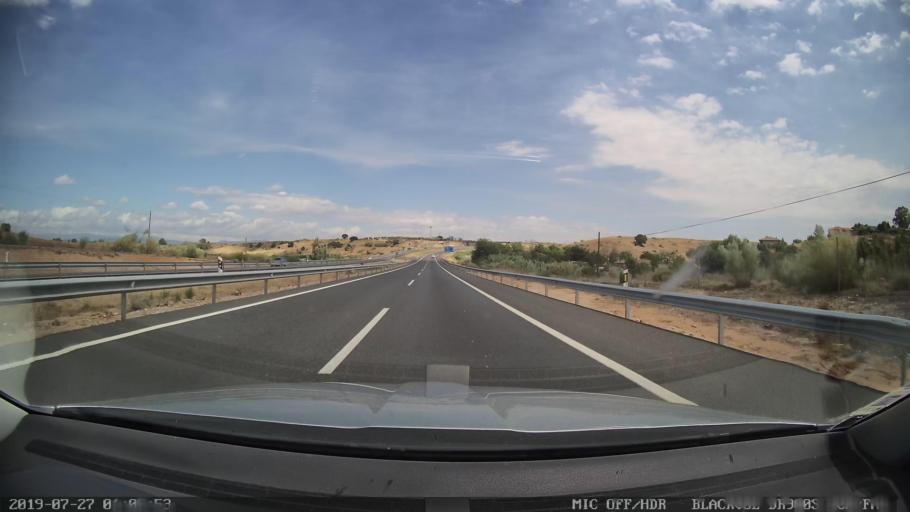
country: ES
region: Castille-La Mancha
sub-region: Province of Toledo
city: Lucillos
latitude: 40.0075
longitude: -4.6291
